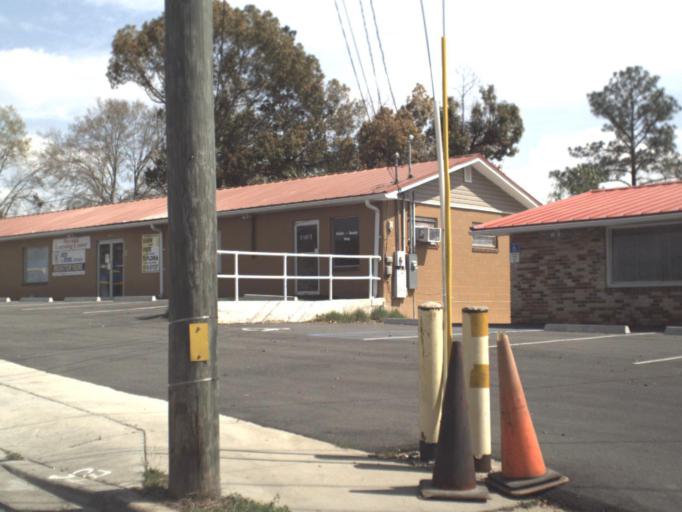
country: US
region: Florida
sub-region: Gadsden County
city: Havana
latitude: 30.6196
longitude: -84.4152
